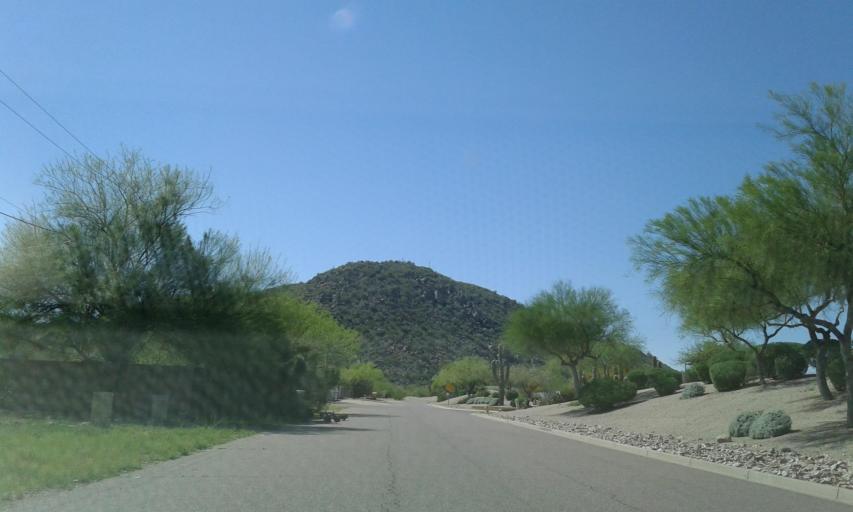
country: US
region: Arizona
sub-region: Maricopa County
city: Cave Creek
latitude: 33.6804
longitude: -112.0345
